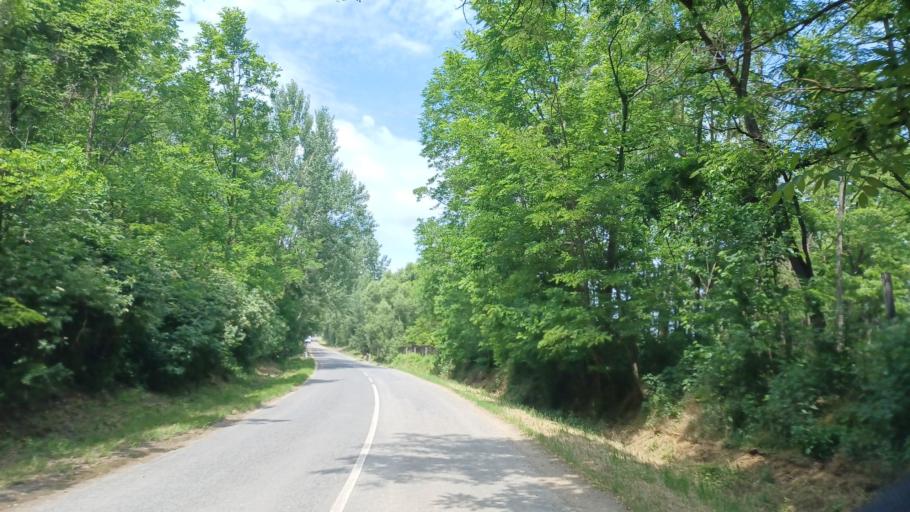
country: HU
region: Tolna
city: Simontornya
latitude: 46.6910
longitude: 18.5213
